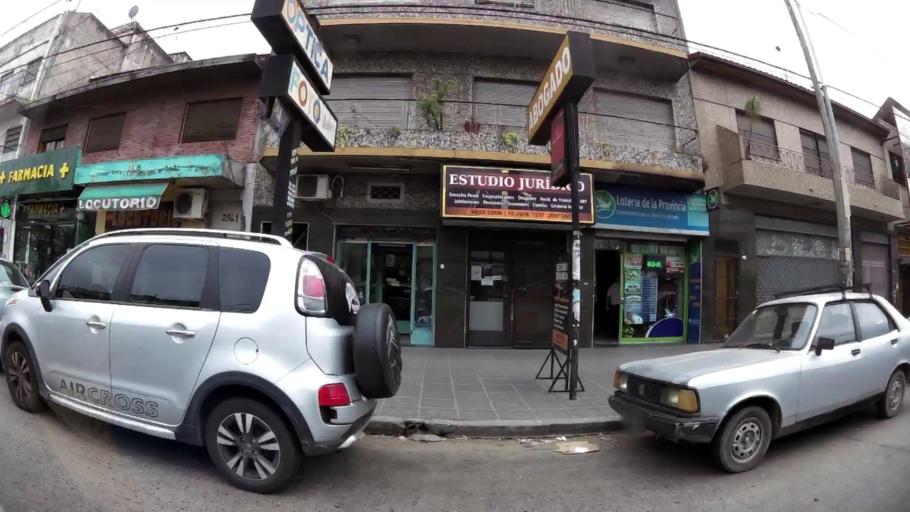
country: AR
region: Buenos Aires
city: San Justo
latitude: -34.6871
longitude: -58.5217
